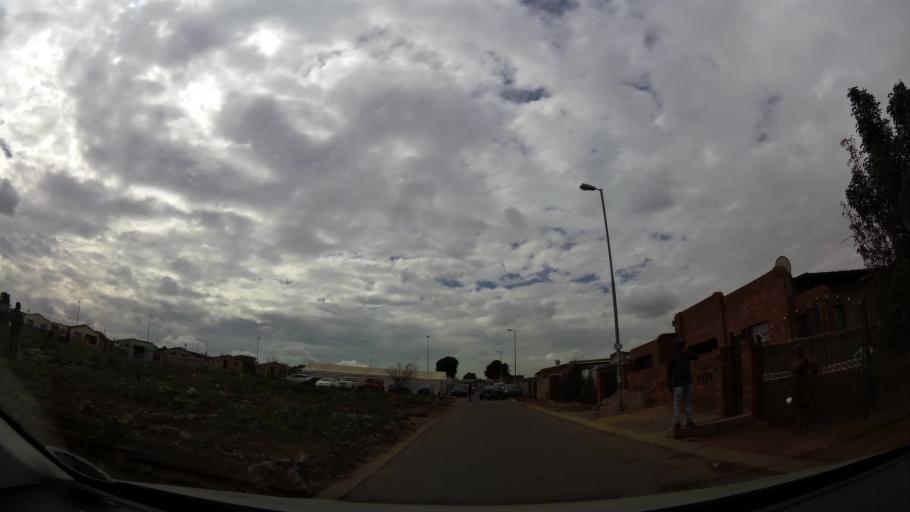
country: ZA
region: Gauteng
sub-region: City of Johannesburg Metropolitan Municipality
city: Soweto
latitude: -26.2812
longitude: 27.8557
